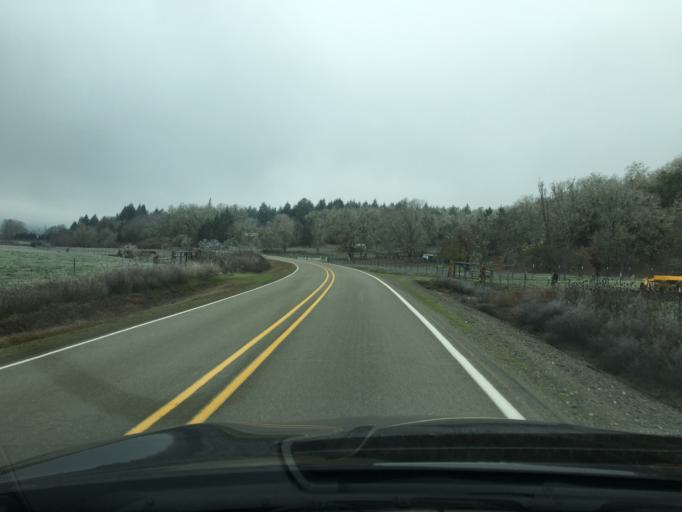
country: US
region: Oregon
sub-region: Douglas County
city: Sutherlin
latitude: 43.3742
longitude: -123.4655
